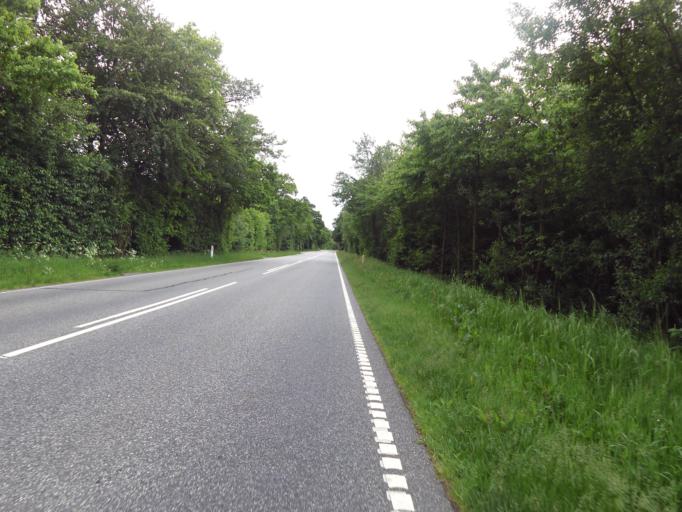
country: DK
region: South Denmark
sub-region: Haderslev Kommune
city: Gram
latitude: 55.3055
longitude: 9.0619
